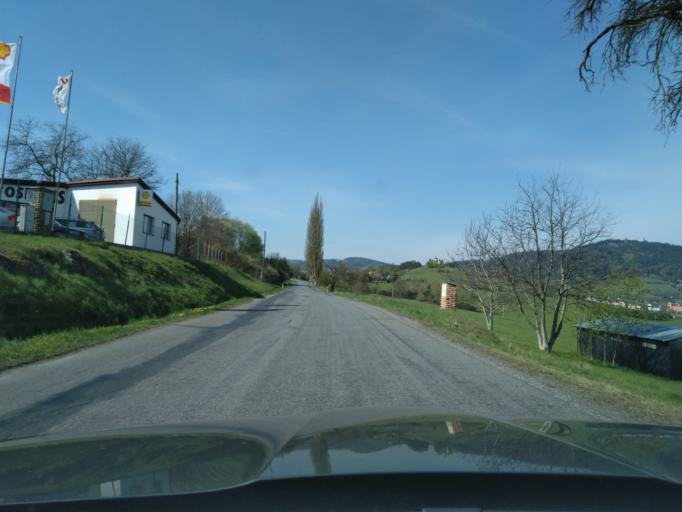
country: CZ
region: Plzensky
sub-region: Okres Klatovy
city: Susice
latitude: 49.2387
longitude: 13.5391
